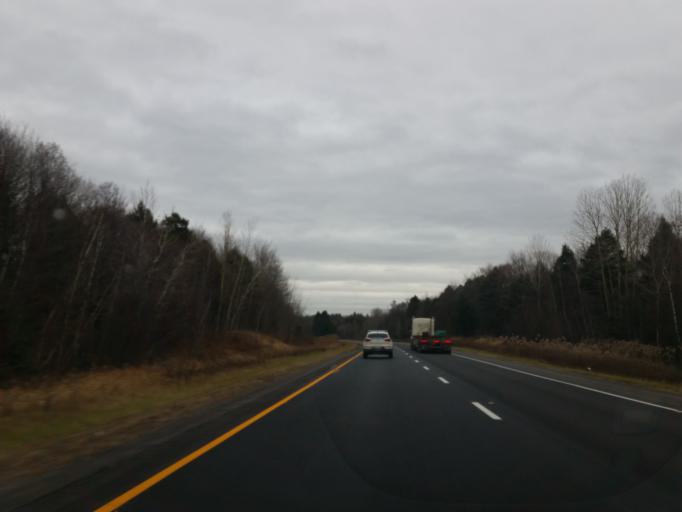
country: CA
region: Quebec
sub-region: Capitale-Nationale
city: Saint-Marc-des-Carrieres
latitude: 46.6025
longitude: -72.0643
